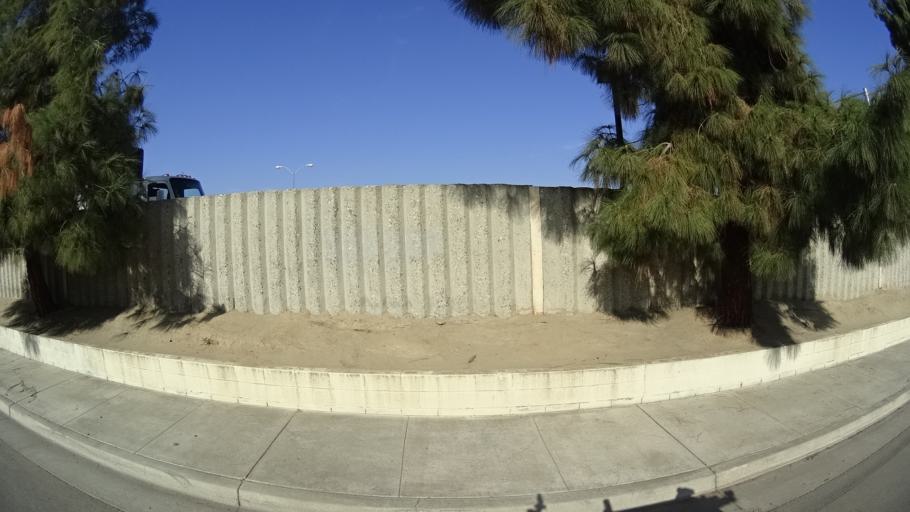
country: US
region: California
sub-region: Kern County
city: Bakersfield
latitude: 35.3376
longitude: -119.0500
